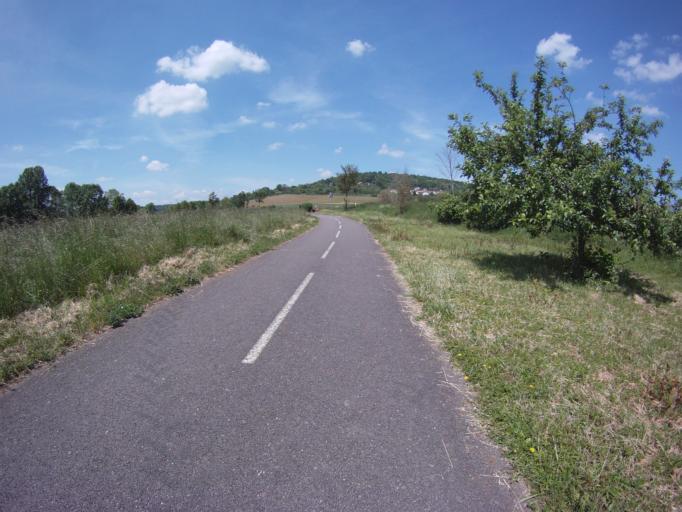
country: FR
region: Lorraine
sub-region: Departement de Meurthe-et-Moselle
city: Eulmont
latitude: 48.7420
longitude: 6.2211
